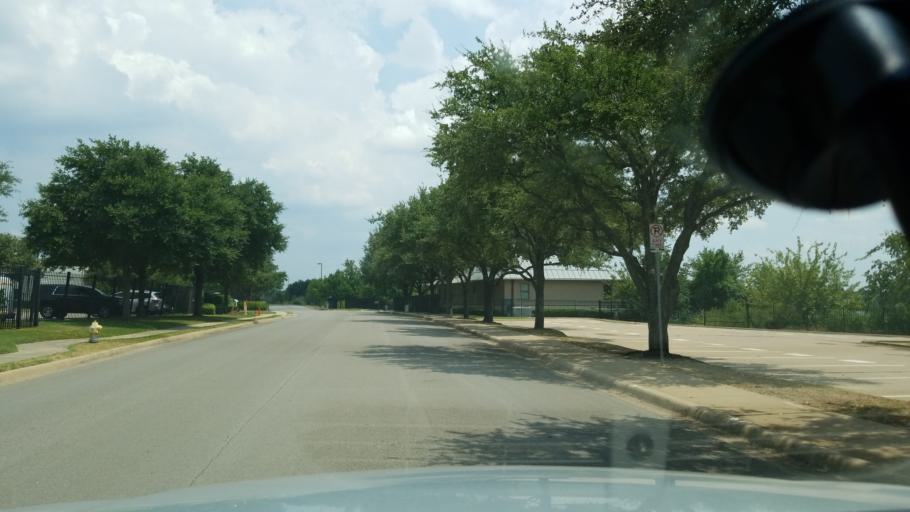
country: US
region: Texas
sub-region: Dallas County
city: Irving
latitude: 32.8570
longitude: -96.8996
